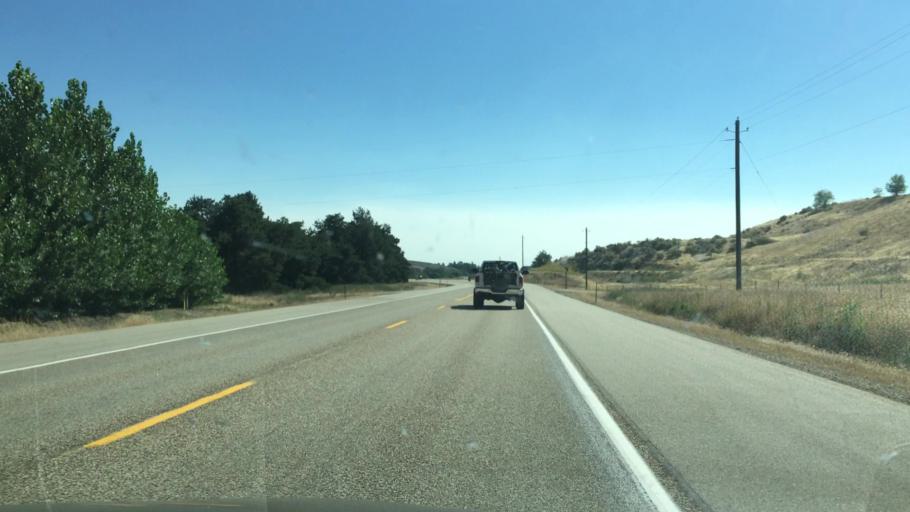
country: US
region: Idaho
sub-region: Ada County
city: Eagle
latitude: 43.7405
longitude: -116.3018
